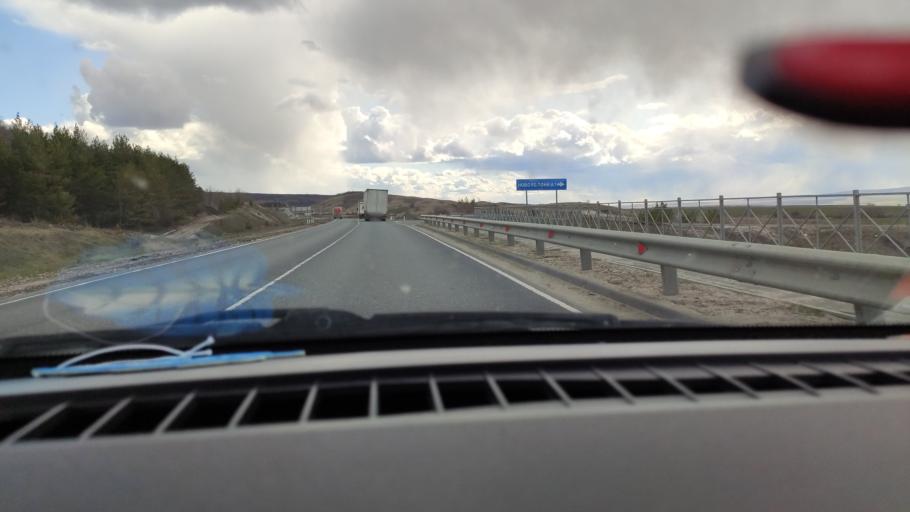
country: RU
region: Saratov
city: Alekseyevka
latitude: 52.3837
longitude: 47.9736
